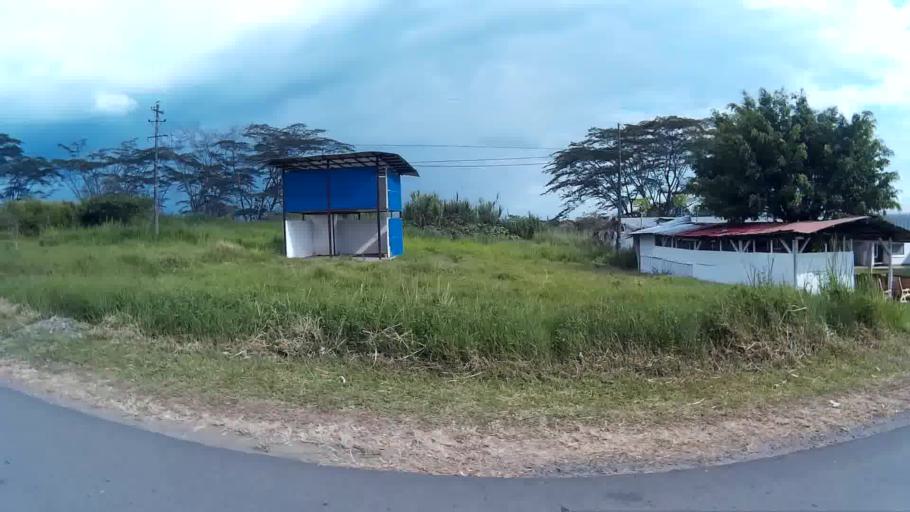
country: CO
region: Valle del Cauca
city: Cartago
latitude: 4.8064
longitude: -75.8170
